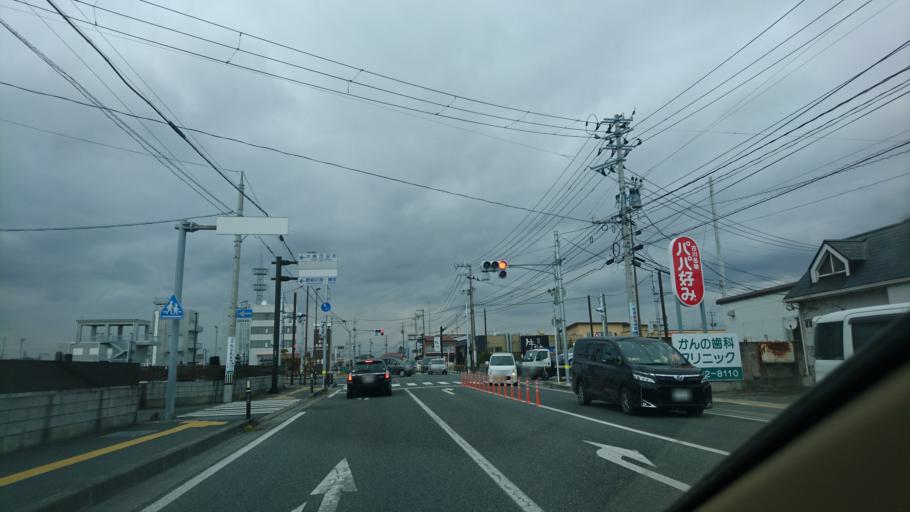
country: JP
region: Miyagi
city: Furukawa
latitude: 38.5801
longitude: 140.9586
